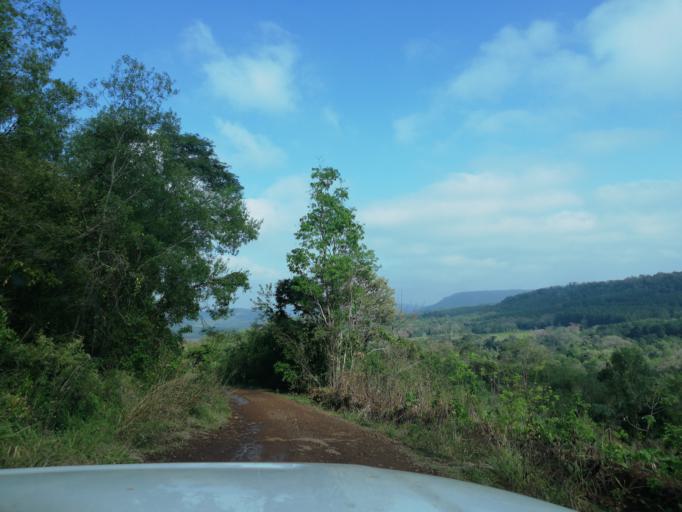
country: AR
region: Misiones
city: Cerro Azul
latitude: -27.5803
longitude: -55.5142
